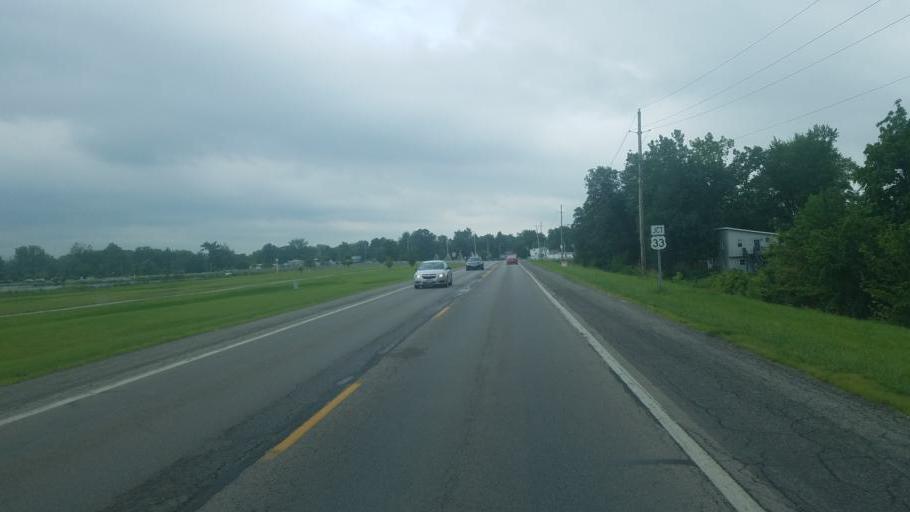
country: US
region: Ohio
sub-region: Logan County
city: Lakeview
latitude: 40.4871
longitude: -83.9220
